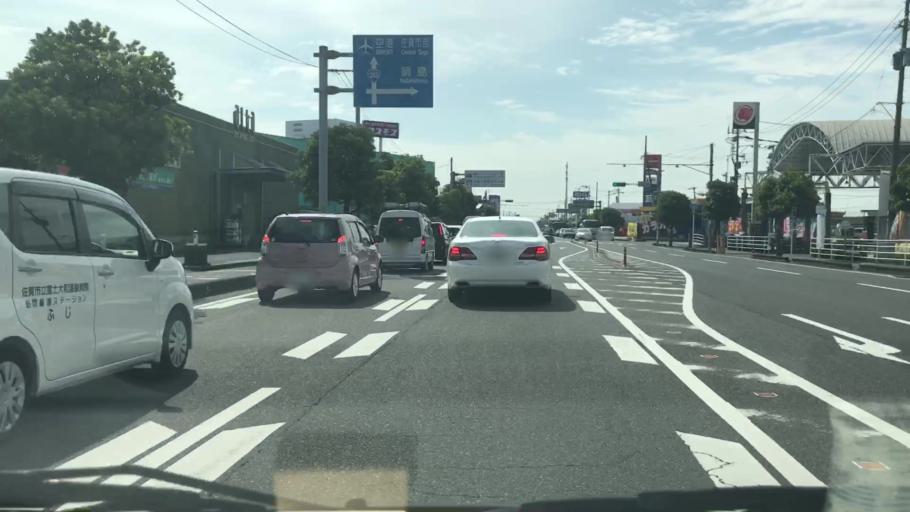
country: JP
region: Saga Prefecture
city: Saga-shi
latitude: 33.2925
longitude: 130.2854
